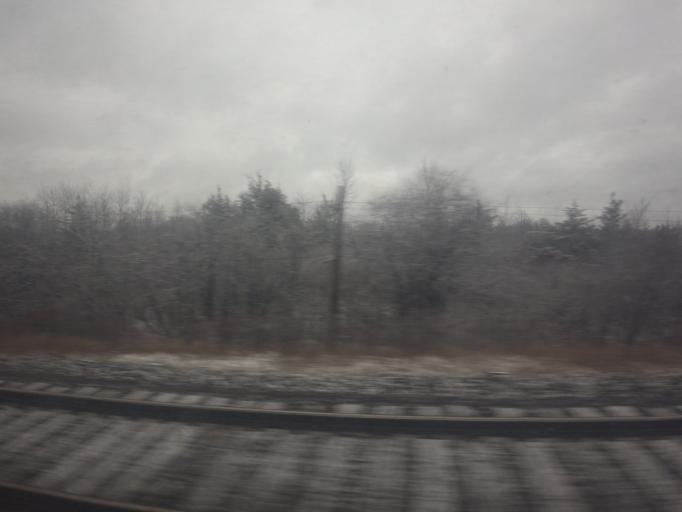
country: US
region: New York
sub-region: Jefferson County
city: Alexandria Bay
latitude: 44.4178
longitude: -75.9932
